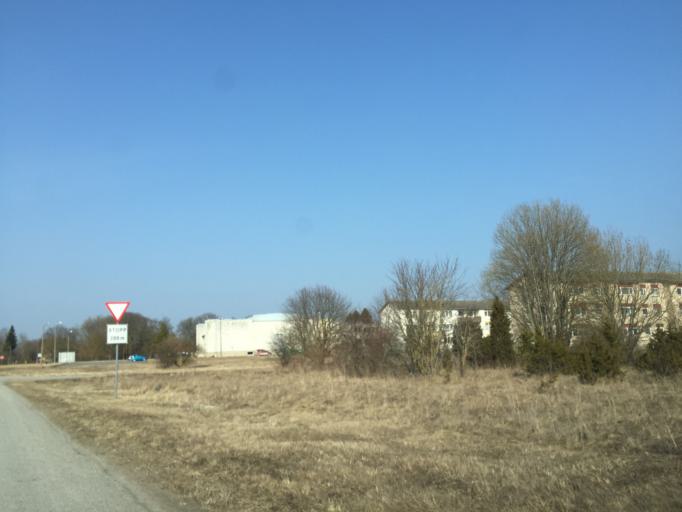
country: EE
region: Saare
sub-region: Orissaare vald
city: Orissaare
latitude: 58.5020
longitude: 23.1141
